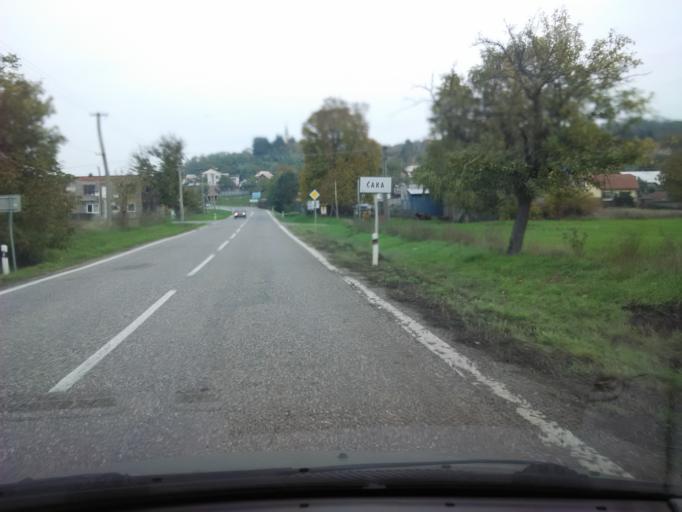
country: SK
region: Nitriansky
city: Svodin
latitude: 48.0374
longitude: 18.4653
